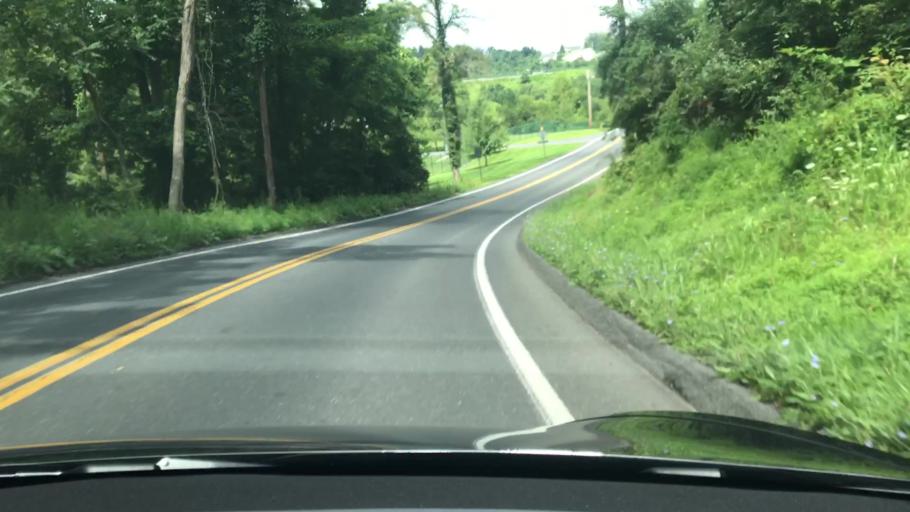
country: US
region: Pennsylvania
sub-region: Cumberland County
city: New Cumberland
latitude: 40.1968
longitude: -76.8774
